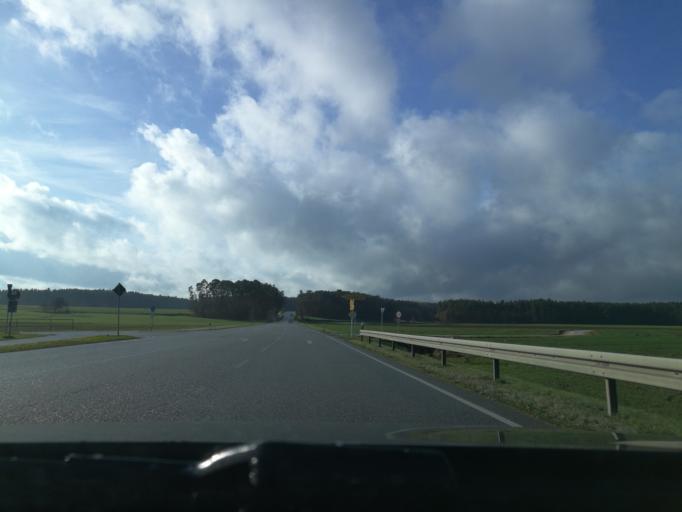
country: DE
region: Bavaria
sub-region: Regierungsbezirk Mittelfranken
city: Kammerstein
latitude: 49.2932
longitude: 10.9627
